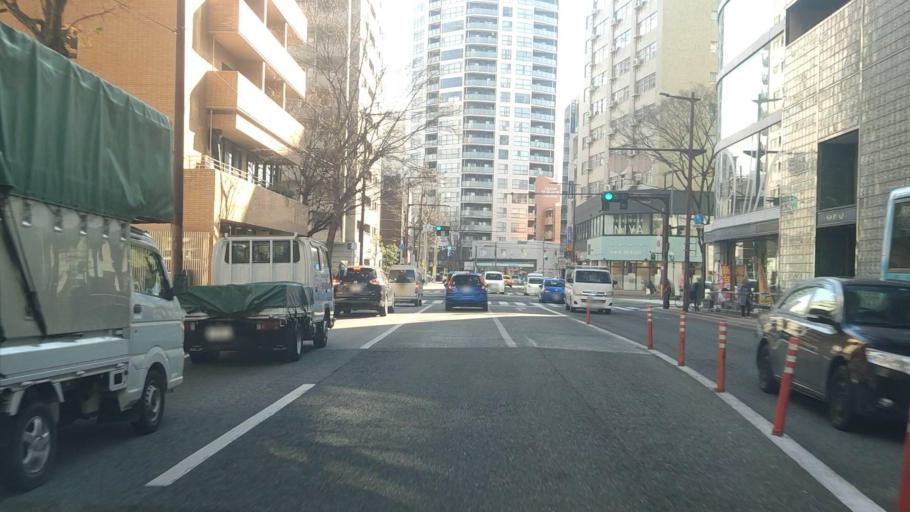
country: JP
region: Fukuoka
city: Fukuoka-shi
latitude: 33.5858
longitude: 130.3914
